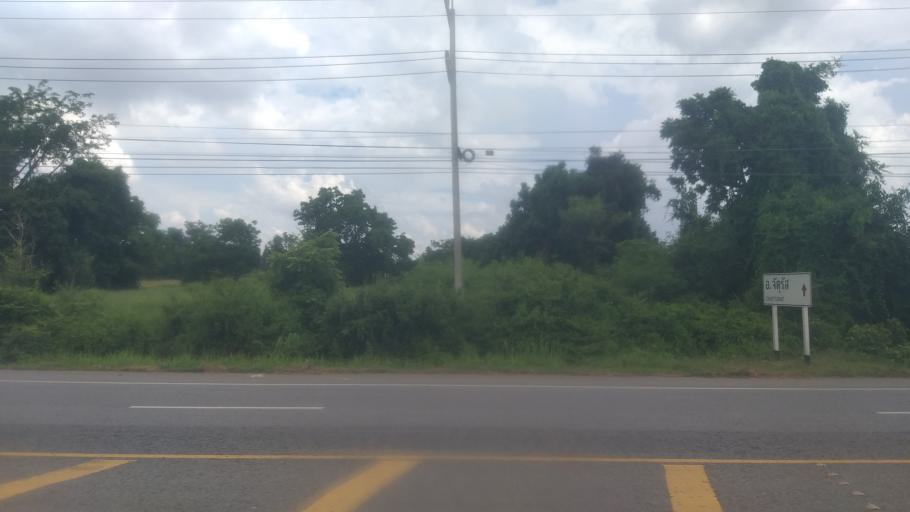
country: TH
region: Chaiyaphum
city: Noen Sa-nga
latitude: 15.6757
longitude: 101.9709
